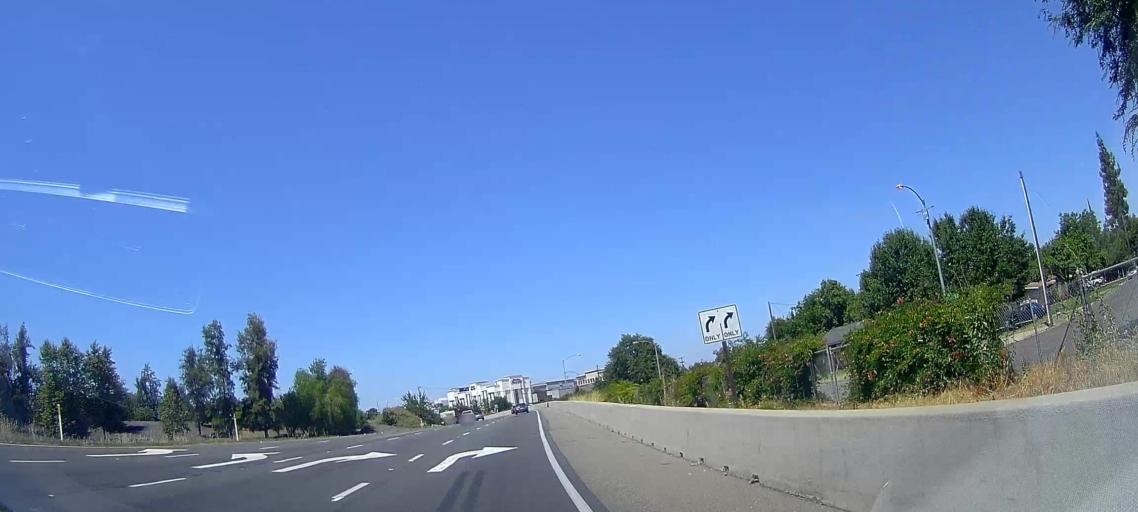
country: US
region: California
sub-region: Fresno County
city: Clovis
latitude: 36.8359
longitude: -119.7841
